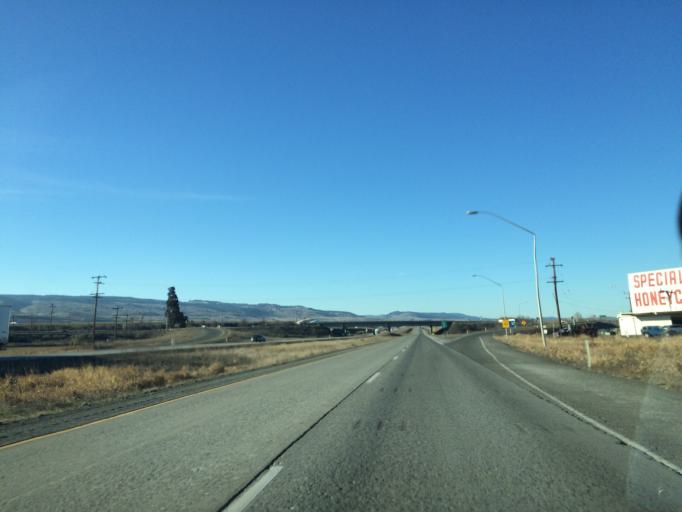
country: US
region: Washington
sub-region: Kittitas County
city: Ellensburg
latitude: 47.0530
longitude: -120.6620
